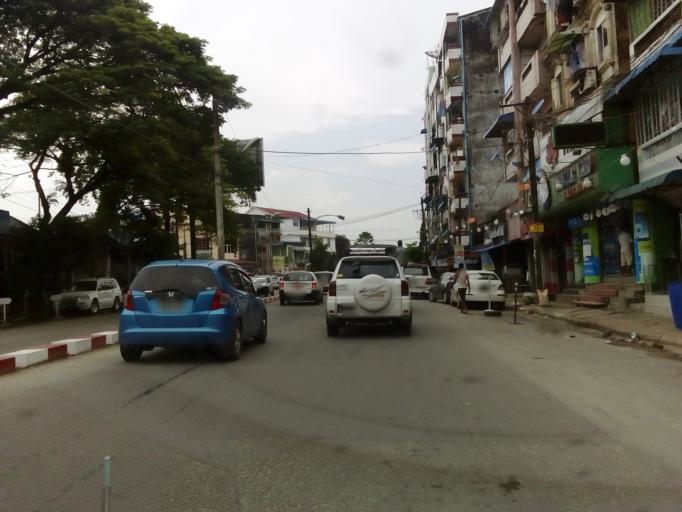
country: MM
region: Yangon
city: Yangon
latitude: 16.8059
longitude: 96.1726
